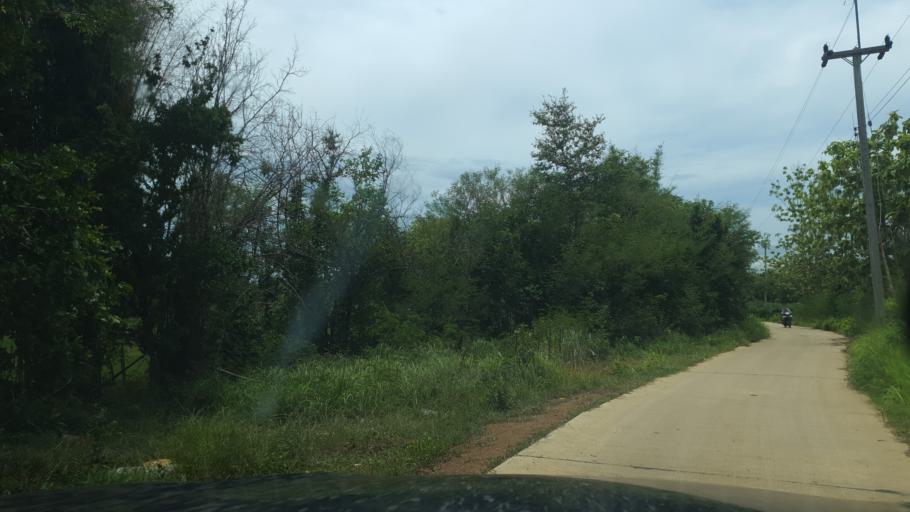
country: TH
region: Lampang
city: Ko Kha
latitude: 18.1306
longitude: 99.3373
